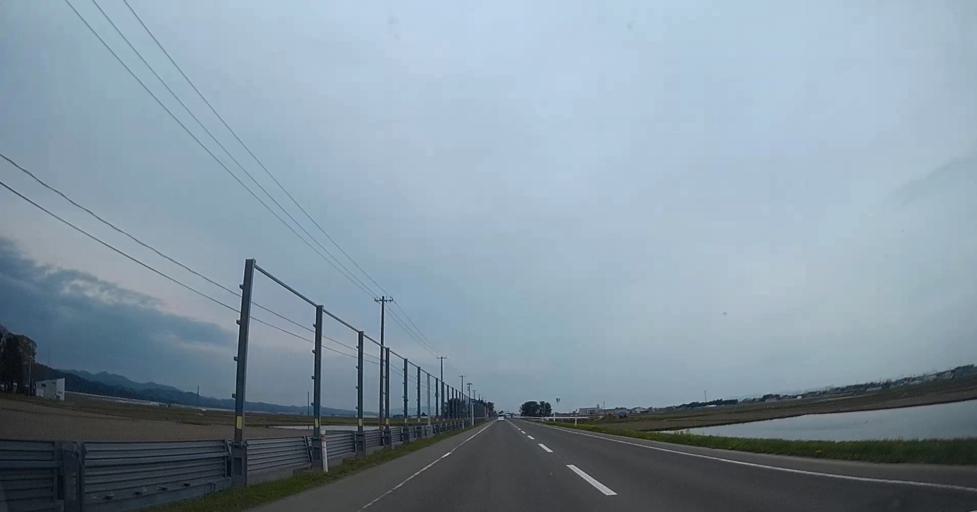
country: JP
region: Aomori
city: Aomori Shi
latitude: 40.8922
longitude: 140.6686
